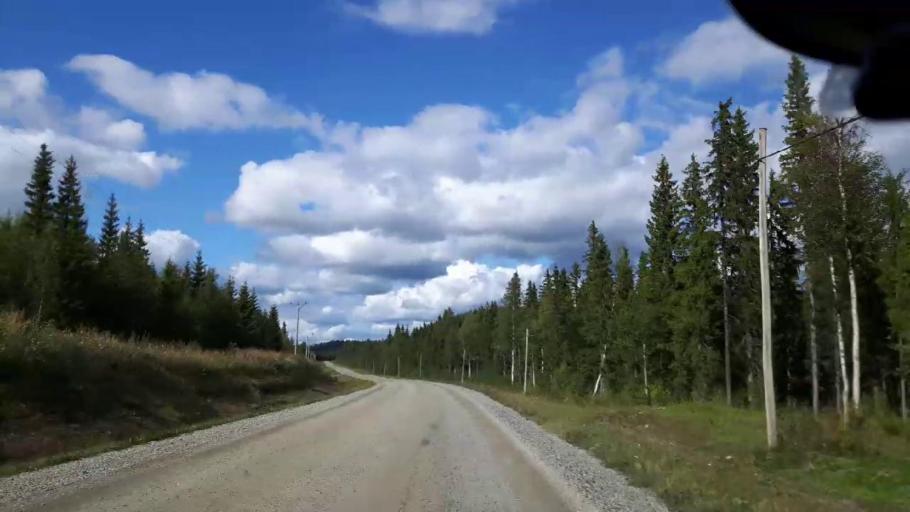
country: SE
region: Jaemtland
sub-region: Stroemsunds Kommun
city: Stroemsund
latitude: 63.3158
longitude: 15.5887
